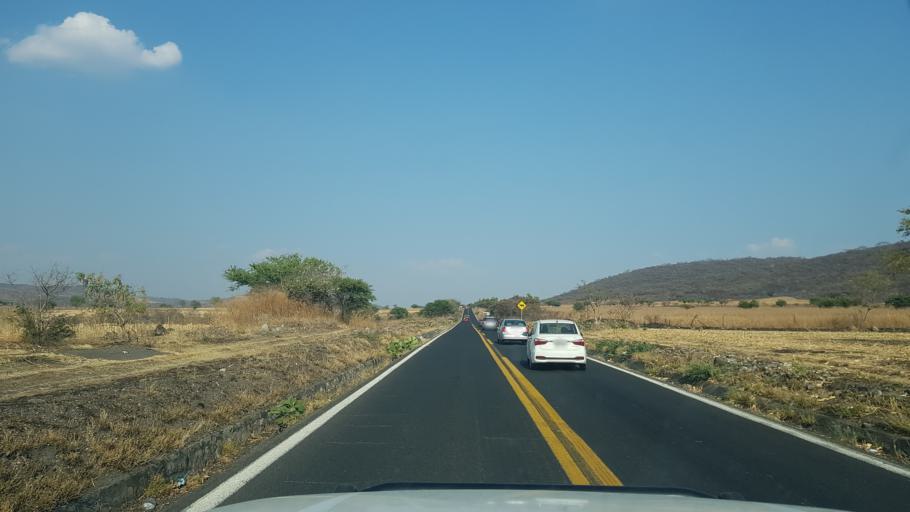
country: MX
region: Puebla
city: Calmeca
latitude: 18.6550
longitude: -98.6616
